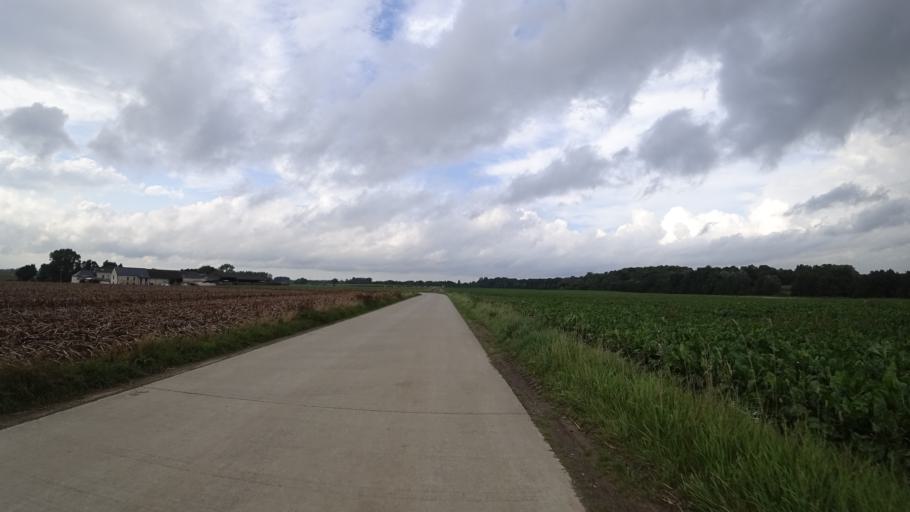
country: BE
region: Wallonia
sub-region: Province de Namur
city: Gembloux
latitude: 50.5491
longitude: 4.7621
